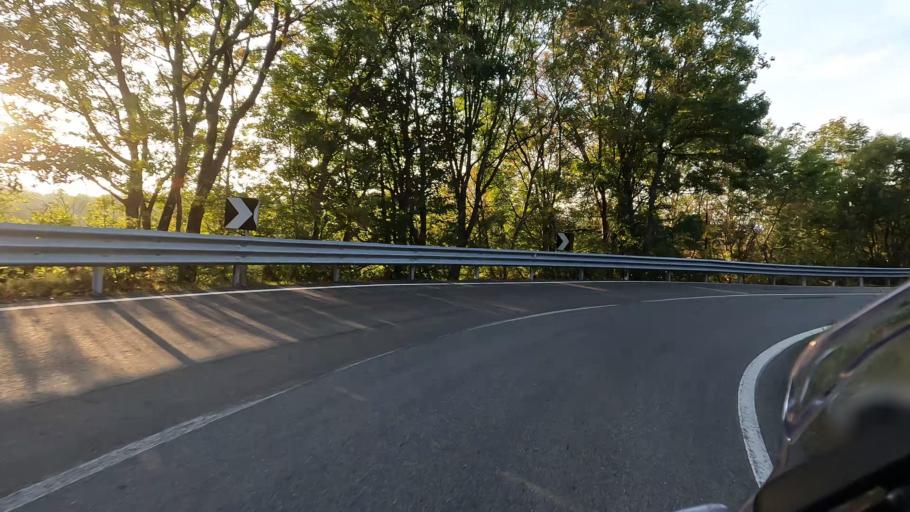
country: IT
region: Liguria
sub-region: Provincia di Savona
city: Sassello
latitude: 44.4907
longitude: 8.4965
